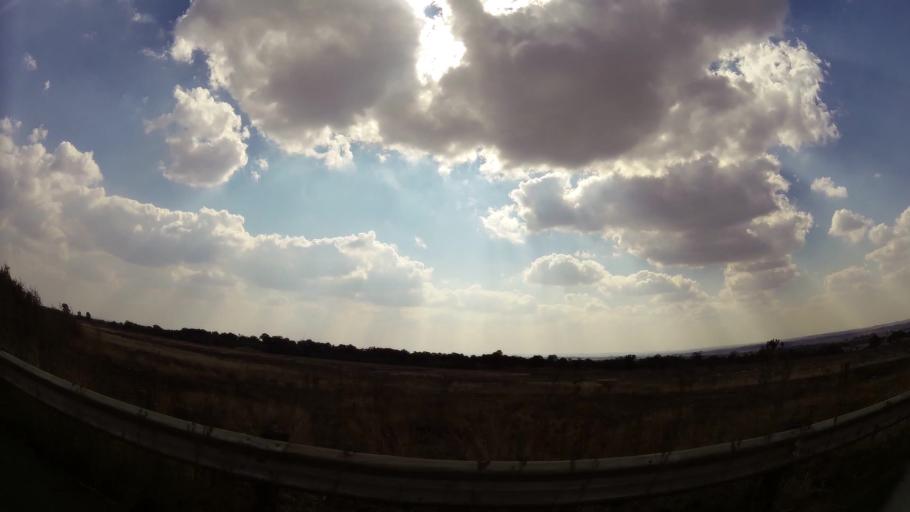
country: ZA
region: Mpumalanga
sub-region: Nkangala District Municipality
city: Delmas
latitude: -26.0942
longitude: 28.6694
